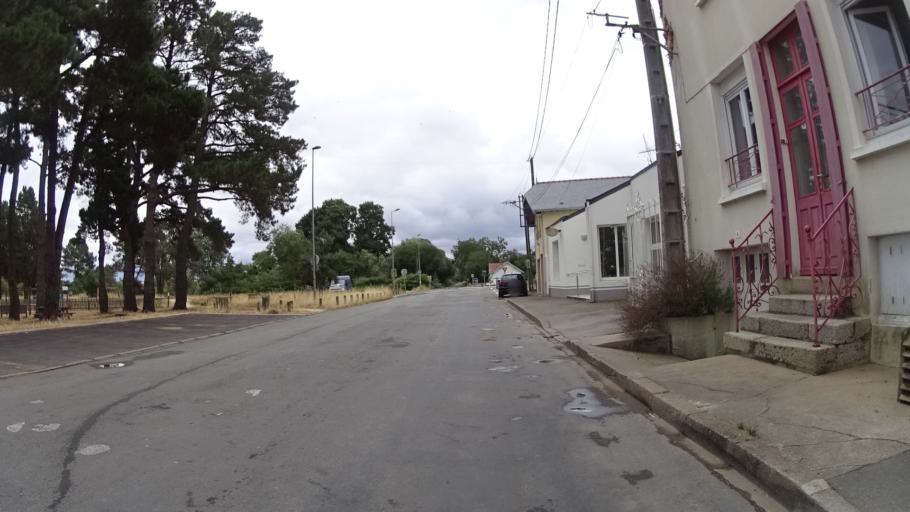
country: FR
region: Pays de la Loire
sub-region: Departement de la Loire-Atlantique
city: Le Pellerin
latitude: 47.2016
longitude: -1.7499
